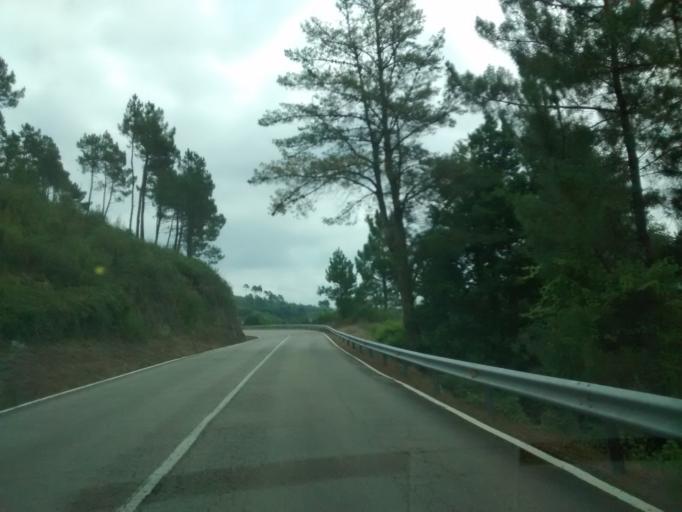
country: ES
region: Galicia
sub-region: Provincia de Ourense
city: Manzaneda
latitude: 42.3348
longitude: -7.1911
